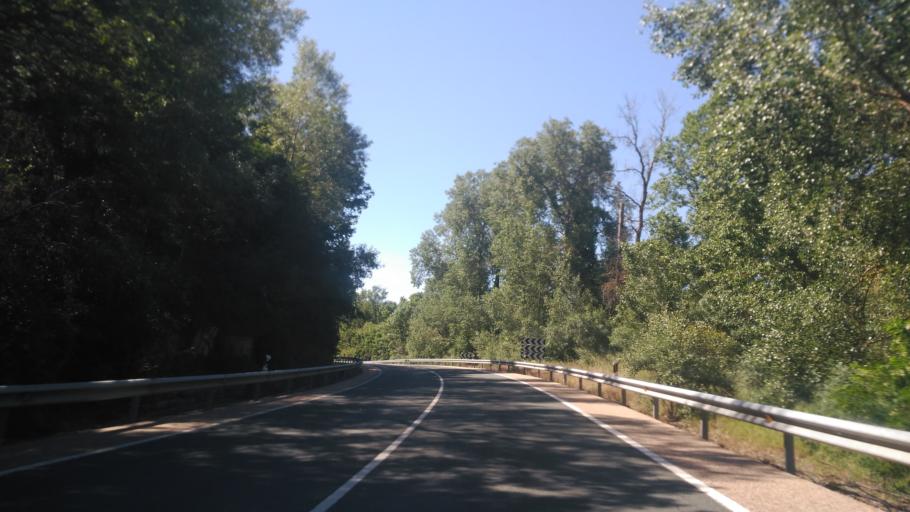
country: ES
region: Castille and Leon
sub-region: Provincia de Zamora
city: Corrales
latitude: 41.3107
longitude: -5.7292
